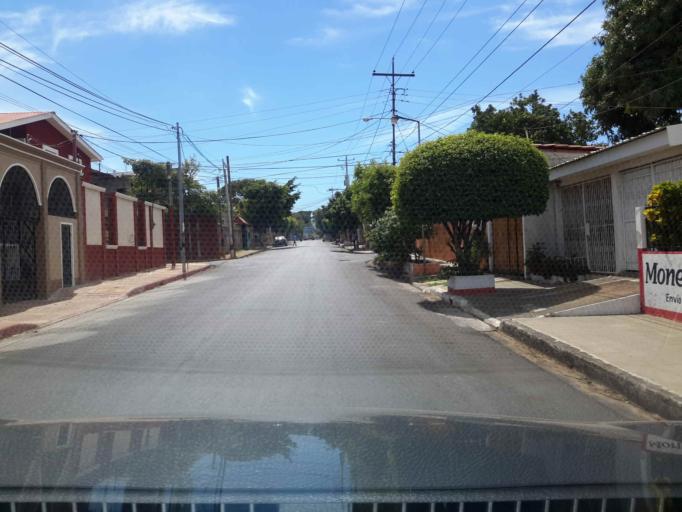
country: NI
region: Managua
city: Managua
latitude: 12.1359
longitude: -86.2927
